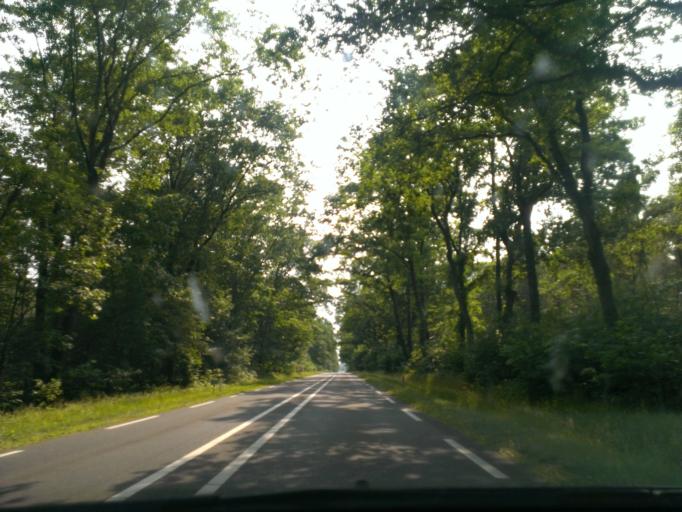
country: NL
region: Overijssel
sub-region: Gemeente Hof van Twente
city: Markelo
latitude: 52.2932
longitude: 6.4536
